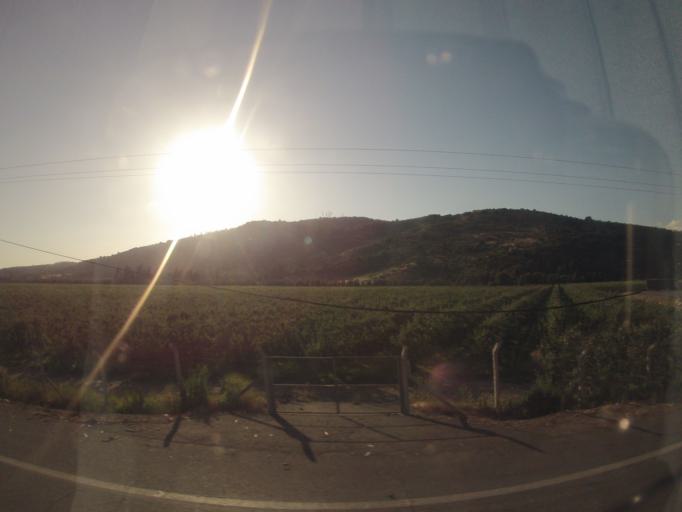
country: CL
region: O'Higgins
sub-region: Provincia de Colchagua
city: Chimbarongo
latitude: -34.6329
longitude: -70.9901
